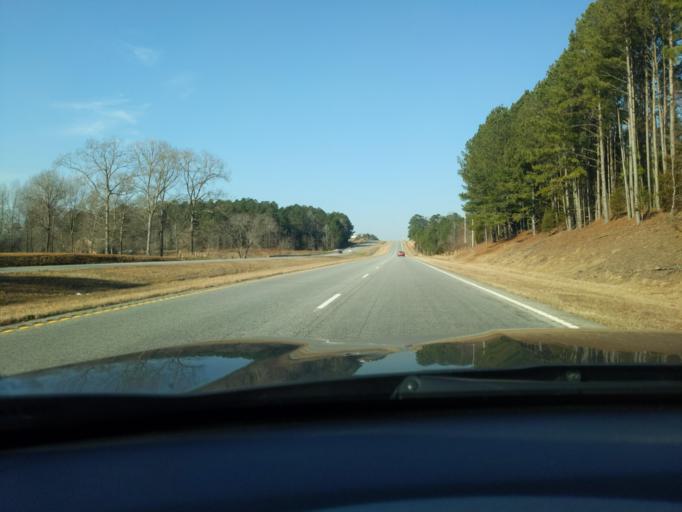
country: US
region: South Carolina
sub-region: Abbeville County
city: Abbeville
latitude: 34.1838
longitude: -82.3123
